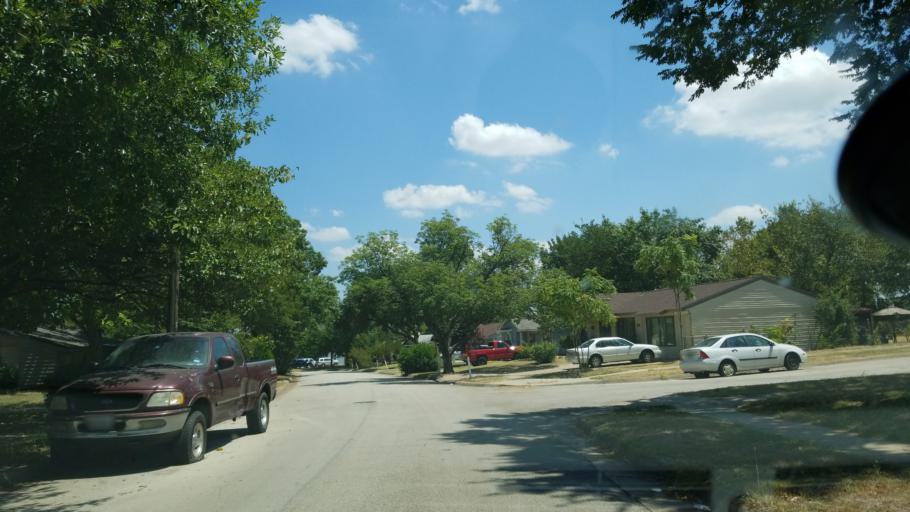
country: US
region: Texas
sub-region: Dallas County
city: Duncanville
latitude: 32.6642
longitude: -96.8943
